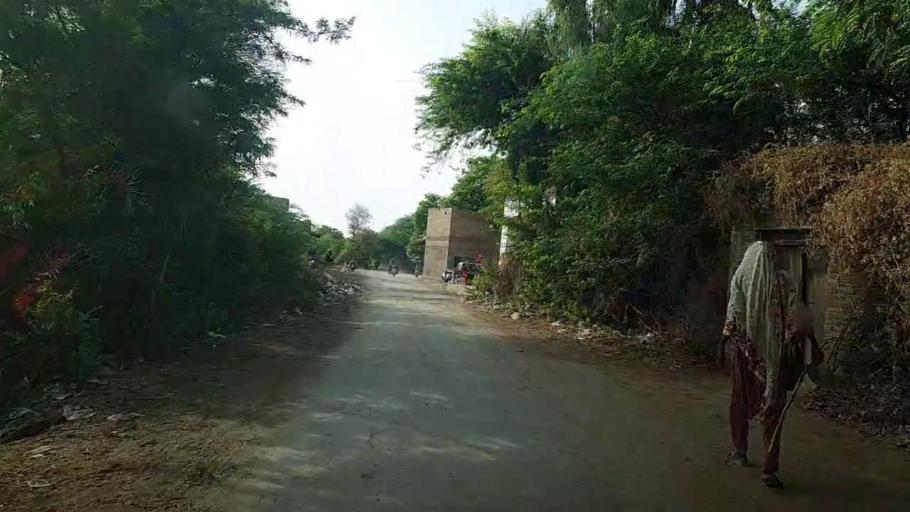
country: PK
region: Sindh
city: Khairpur Nathan Shah
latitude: 27.1176
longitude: 67.7882
